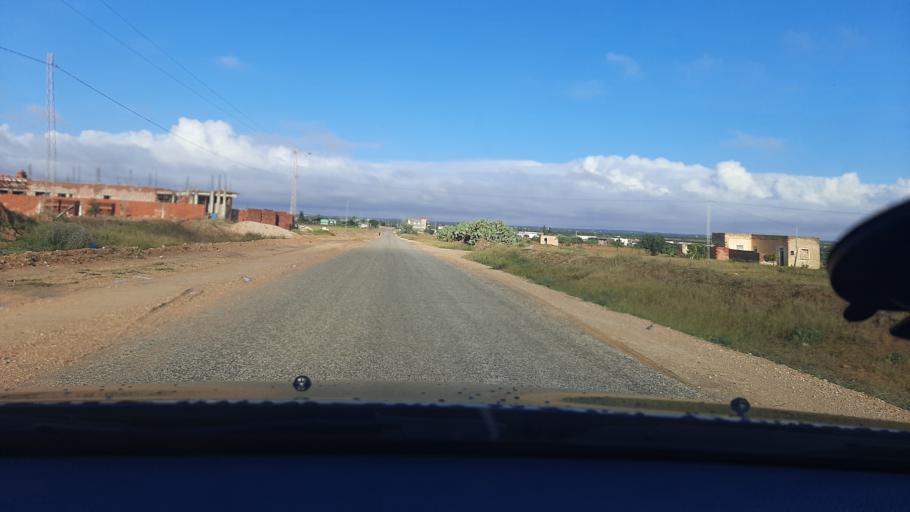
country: TN
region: Safaqis
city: Sfax
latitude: 34.8828
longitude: 10.6302
